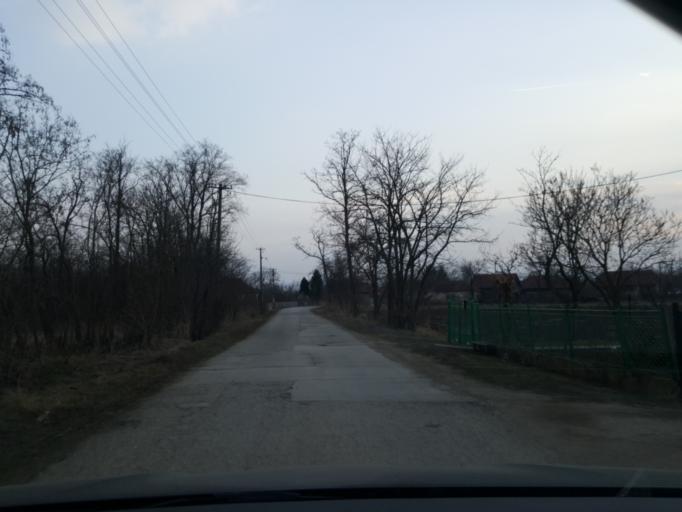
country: RS
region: Central Serbia
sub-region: Nisavski Okrug
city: Aleksinac
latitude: 43.5823
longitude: 21.6472
